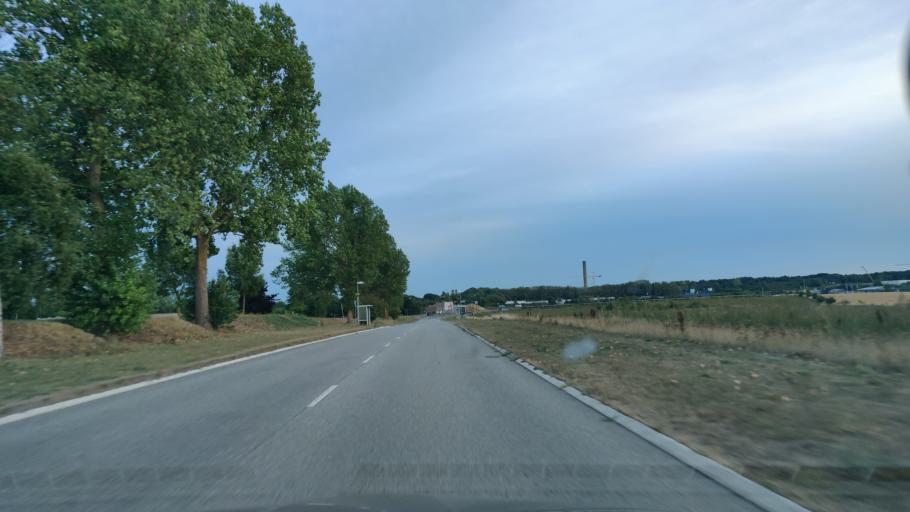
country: DK
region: Capital Region
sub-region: Hoje-Taastrup Kommune
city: Flong
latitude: 55.6601
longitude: 12.1756
